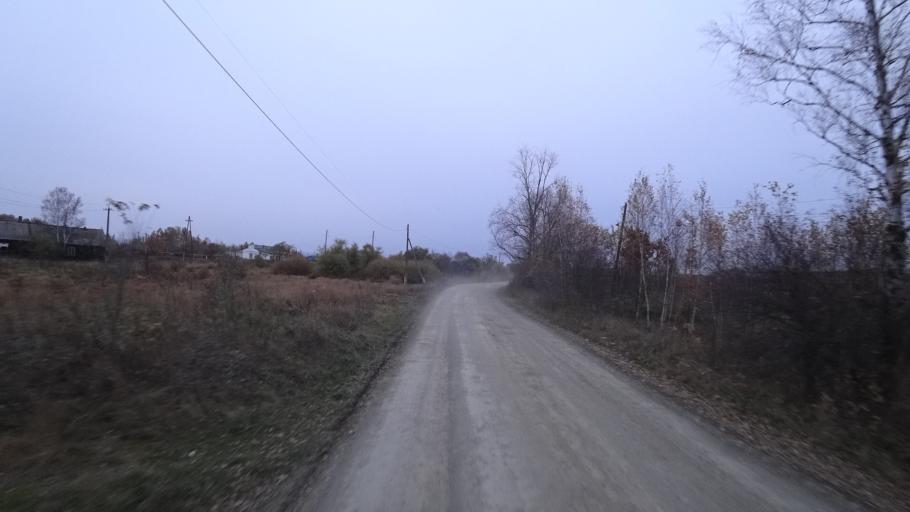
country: RU
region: Khabarovsk Krai
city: Amursk
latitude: 49.9022
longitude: 136.1429
